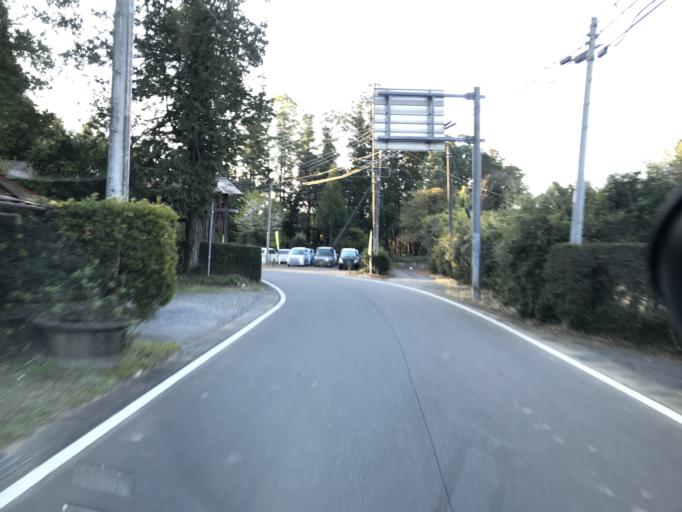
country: JP
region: Chiba
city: Yokaichiba
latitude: 35.7703
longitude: 140.5353
